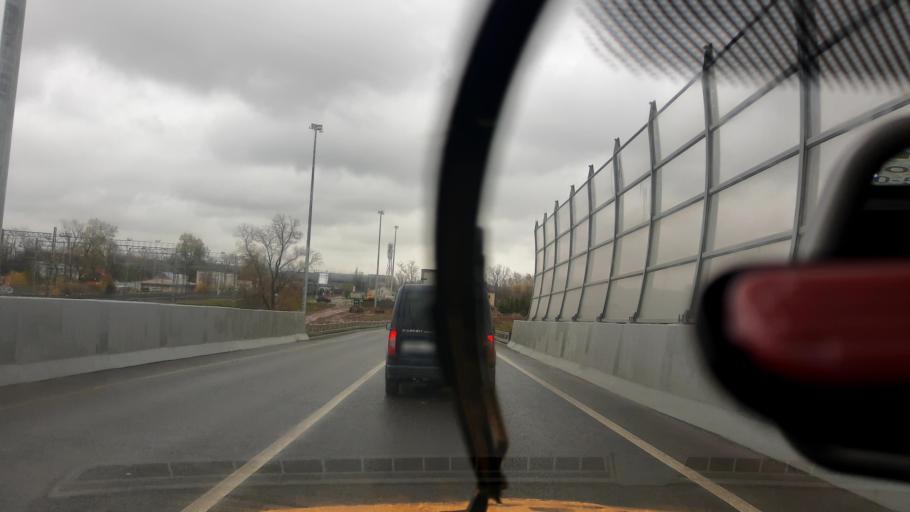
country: RU
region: Moskovskaya
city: Odintsovo
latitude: 55.6488
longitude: 37.2614
